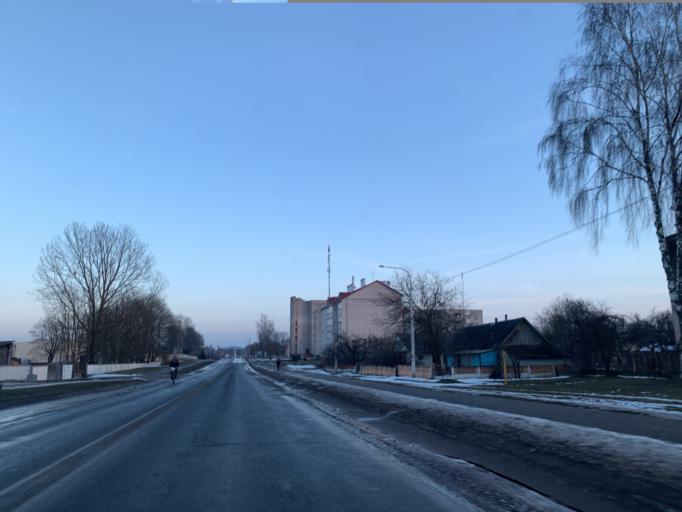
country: BY
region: Minsk
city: Nyasvizh
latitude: 53.2312
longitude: 26.6562
